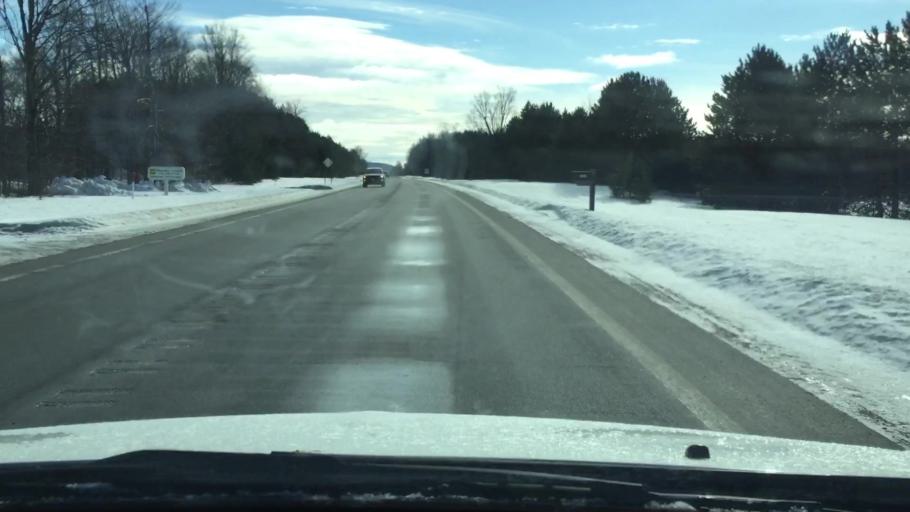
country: US
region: Michigan
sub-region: Antrim County
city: Mancelona
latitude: 44.9425
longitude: -85.0508
